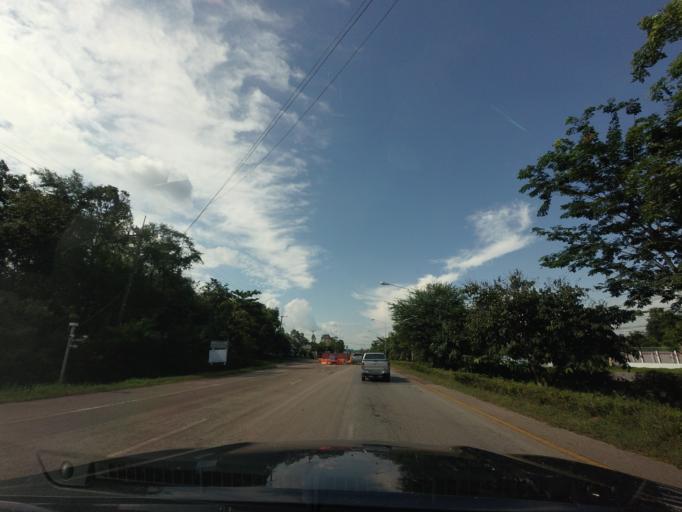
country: TH
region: Nong Khai
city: Sa Khrai
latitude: 17.7611
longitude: 102.7698
